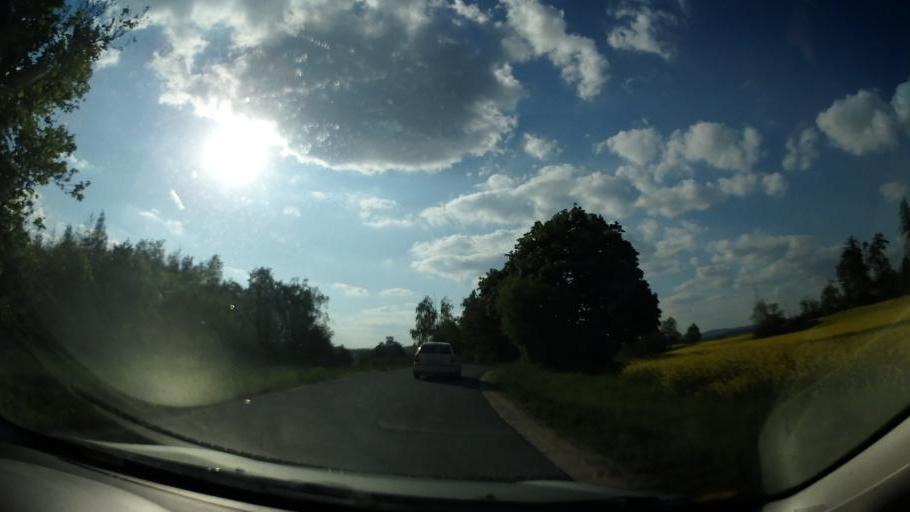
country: CZ
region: Vysocina
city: Budisov
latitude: 49.3116
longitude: 15.9744
